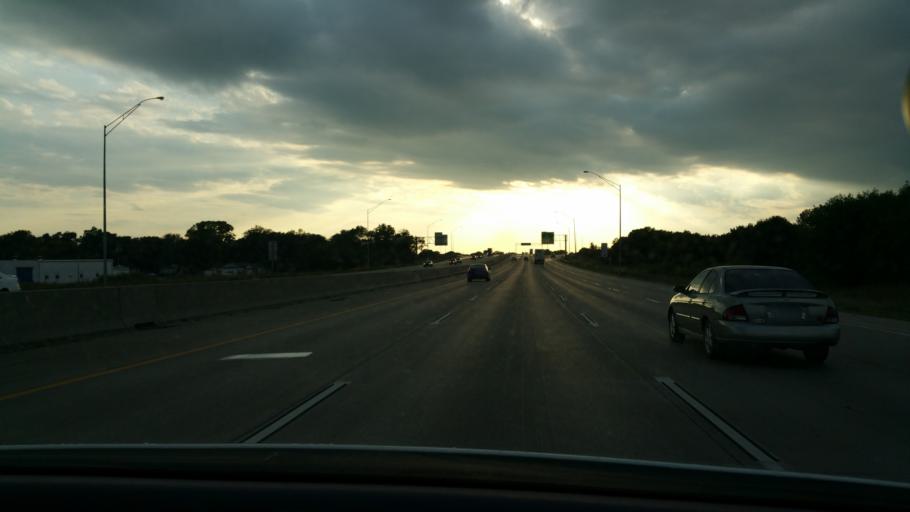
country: US
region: Iowa
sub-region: Polk County
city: Saylorville
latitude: 41.6495
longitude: -93.6087
